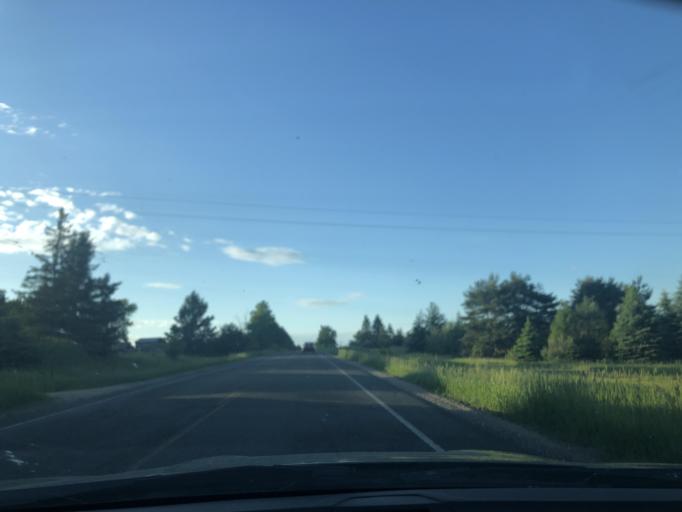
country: US
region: Michigan
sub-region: Missaukee County
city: Lake City
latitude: 44.4006
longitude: -85.0756
